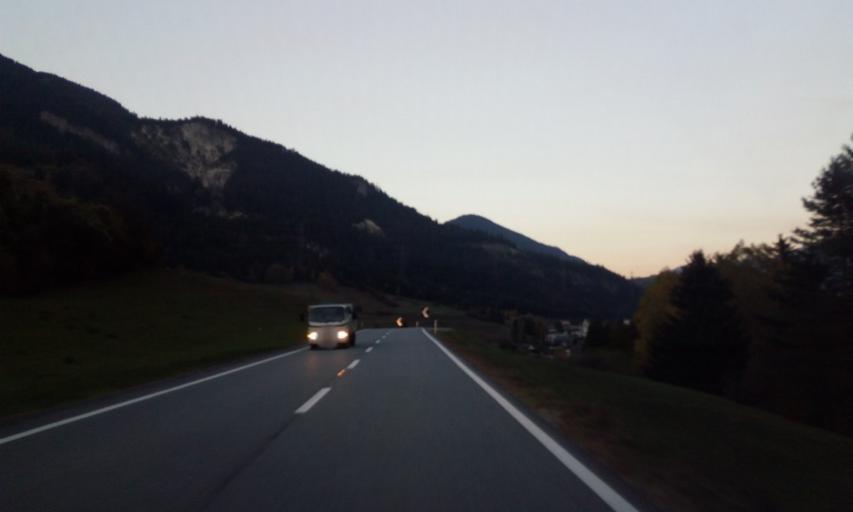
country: CH
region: Grisons
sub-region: Albula District
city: Tiefencastel
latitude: 46.6617
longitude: 9.6028
